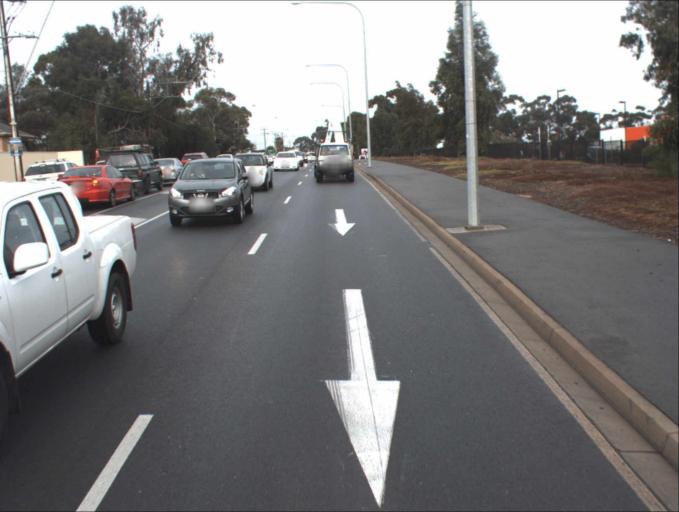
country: AU
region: South Australia
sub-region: Salisbury
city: Ingle Farm
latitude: -34.8433
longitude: 138.6202
